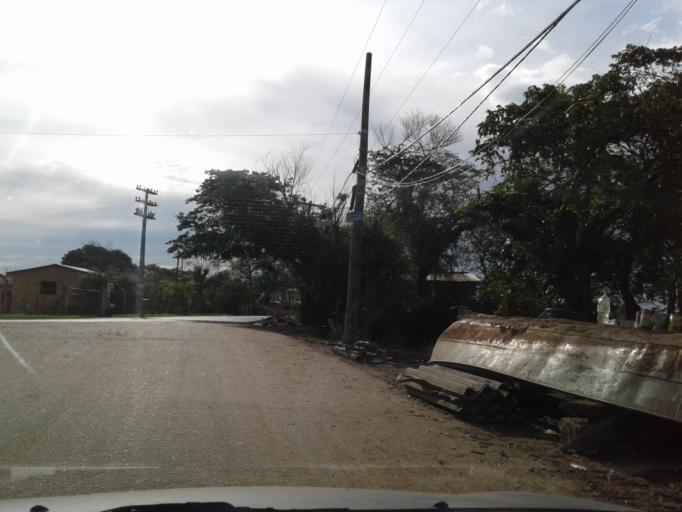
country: BR
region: Rio Grande do Sul
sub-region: Porto Alegre
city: Porto Alegre
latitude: -30.0238
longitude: -51.2545
